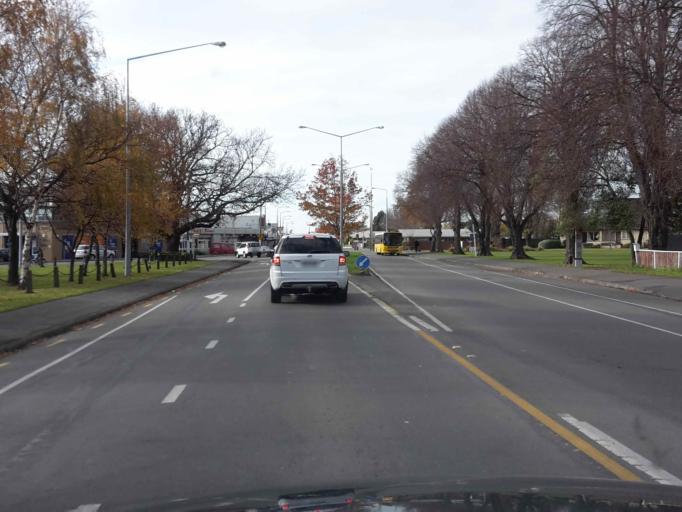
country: NZ
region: Canterbury
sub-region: Christchurch City
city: Christchurch
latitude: -43.5320
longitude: 172.5704
